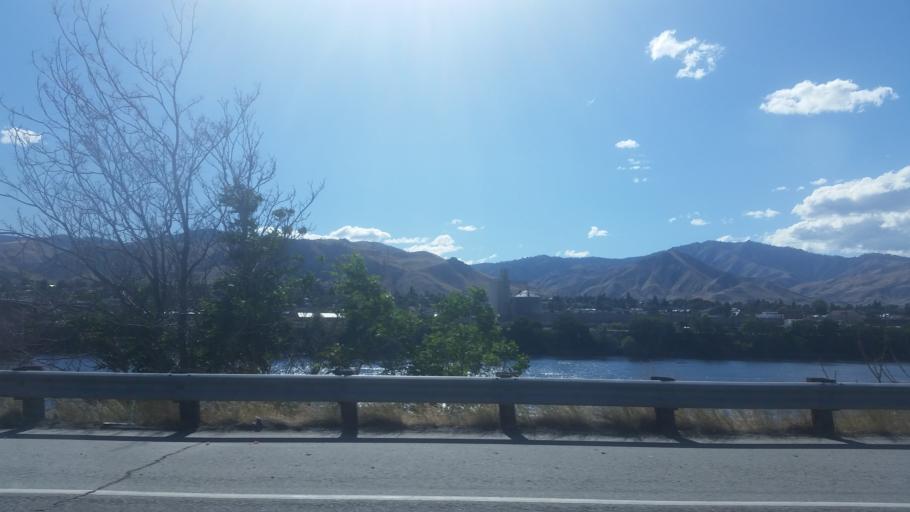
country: US
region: Washington
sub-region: Douglas County
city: East Wenatchee
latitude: 47.4168
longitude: -120.2954
